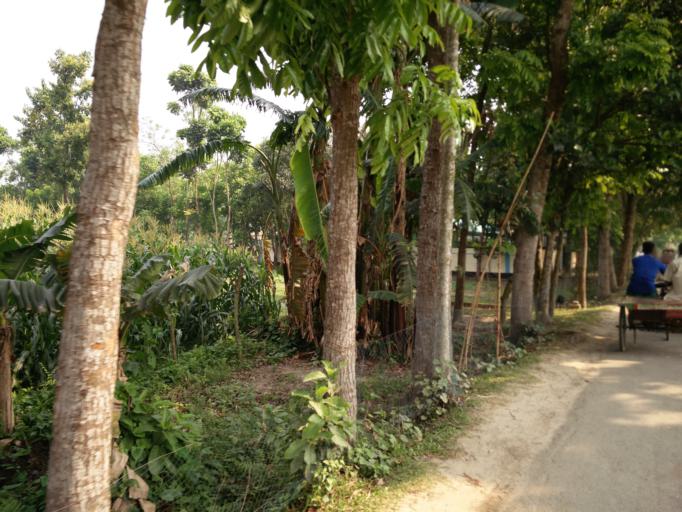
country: BD
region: Dhaka
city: Muktagacha
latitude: 24.9151
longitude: 90.2302
